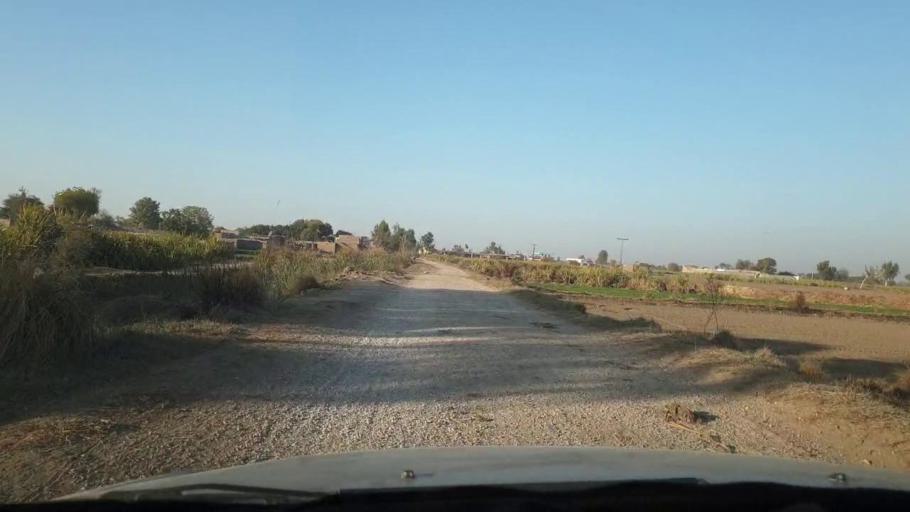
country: PK
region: Sindh
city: Ghotki
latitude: 27.9912
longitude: 69.2726
